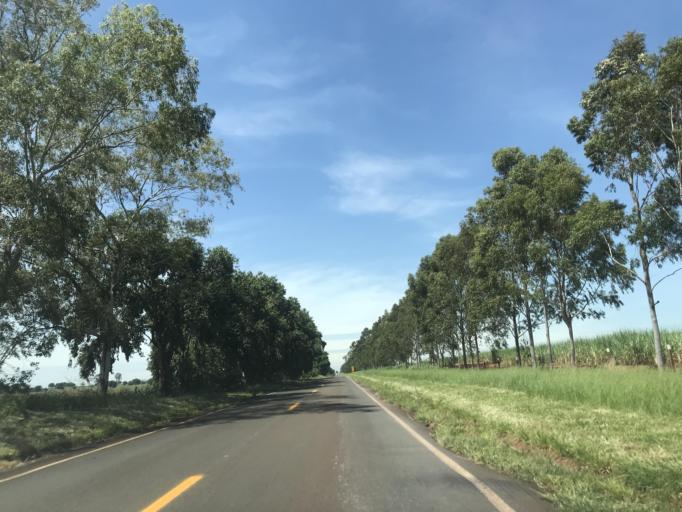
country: BR
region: Parana
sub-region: Paranavai
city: Nova Aurora
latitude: -22.8471
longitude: -52.6574
